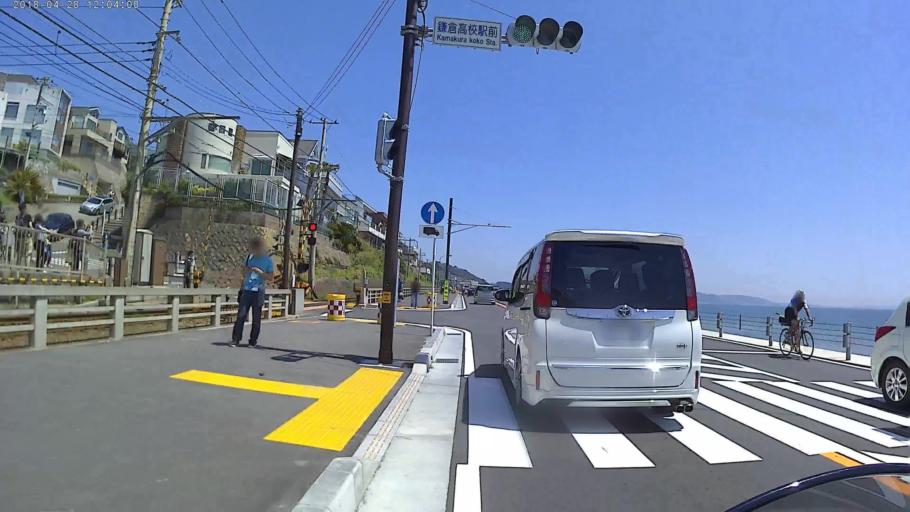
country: JP
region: Kanagawa
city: Fujisawa
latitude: 35.3066
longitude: 139.5018
